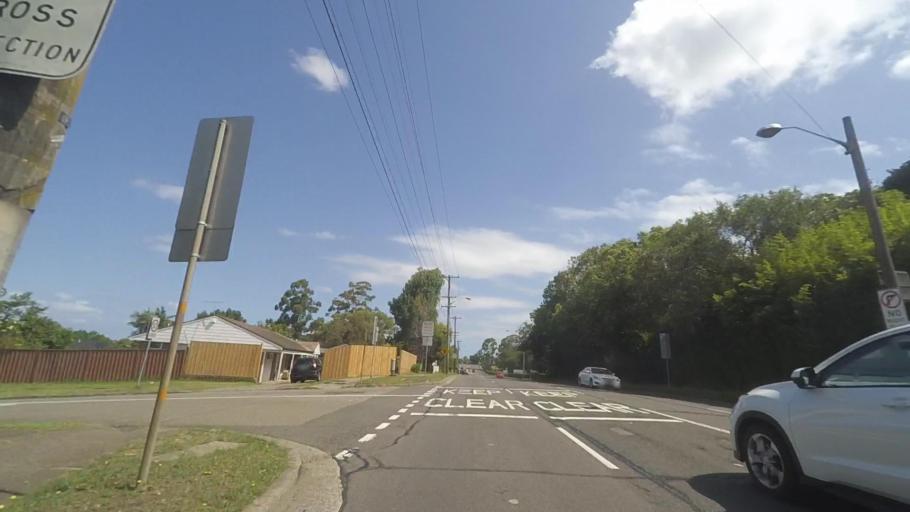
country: AU
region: New South Wales
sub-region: Parramatta
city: Carlingford
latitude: -33.7726
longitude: 151.0512
